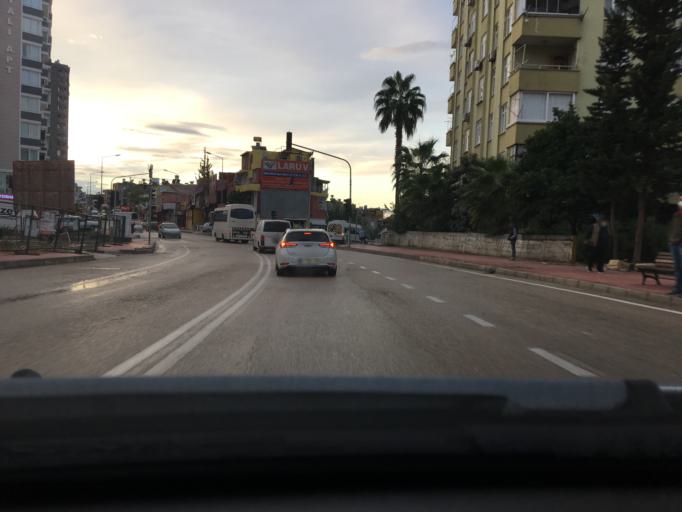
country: TR
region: Adana
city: Seyhan
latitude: 37.0235
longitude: 35.2919
